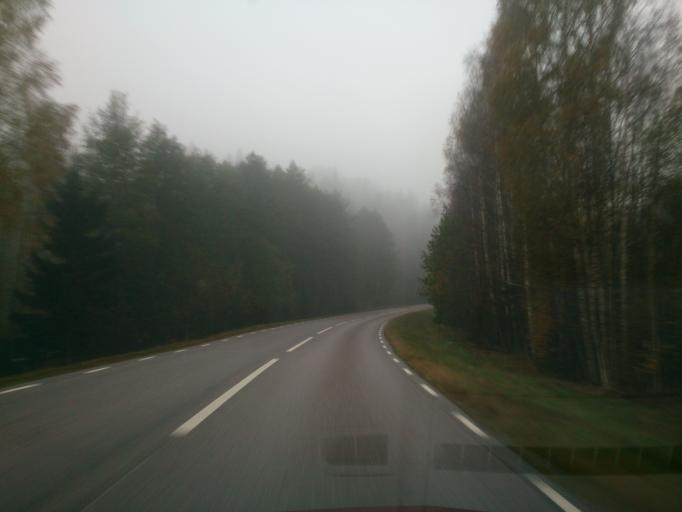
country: SE
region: OEstergoetland
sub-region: Atvidabergs Kommun
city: Atvidaberg
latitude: 58.0835
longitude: 15.9412
